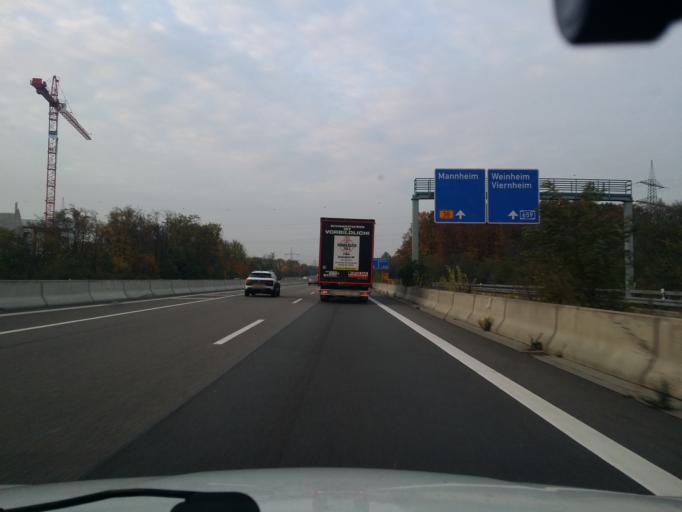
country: DE
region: Hesse
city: Viernheim
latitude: 49.5169
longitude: 8.5603
